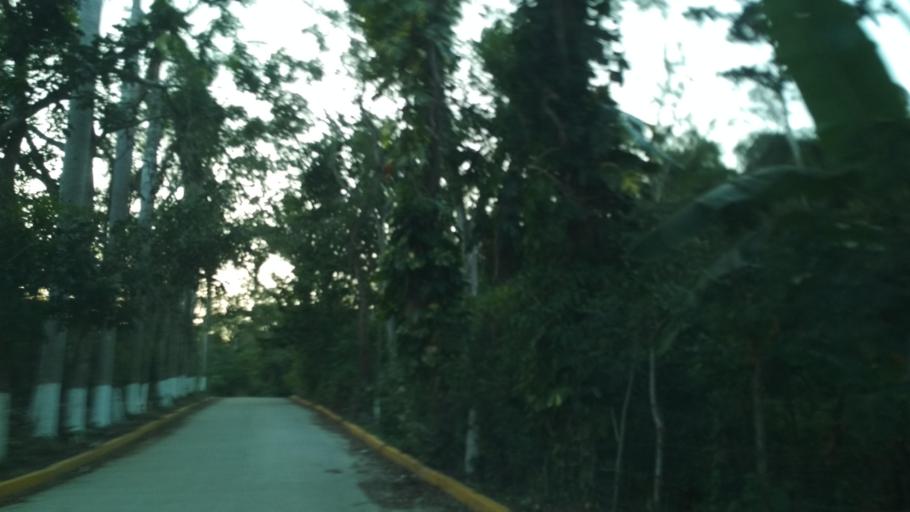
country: MX
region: Veracruz
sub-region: Poza Rica de Hidalgo
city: Arroyo del Maiz Uno
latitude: 20.4774
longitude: -97.3893
